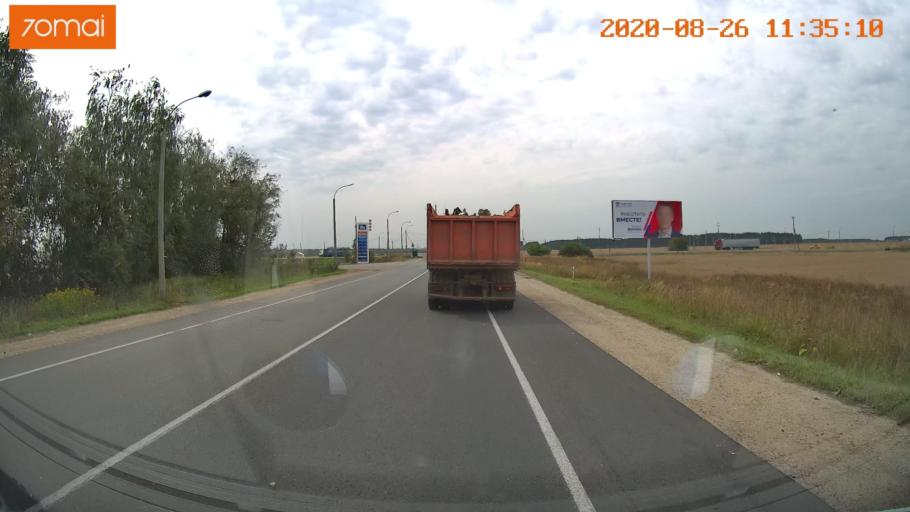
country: RU
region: Rjazan
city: Shilovo
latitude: 54.2776
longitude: 40.8368
